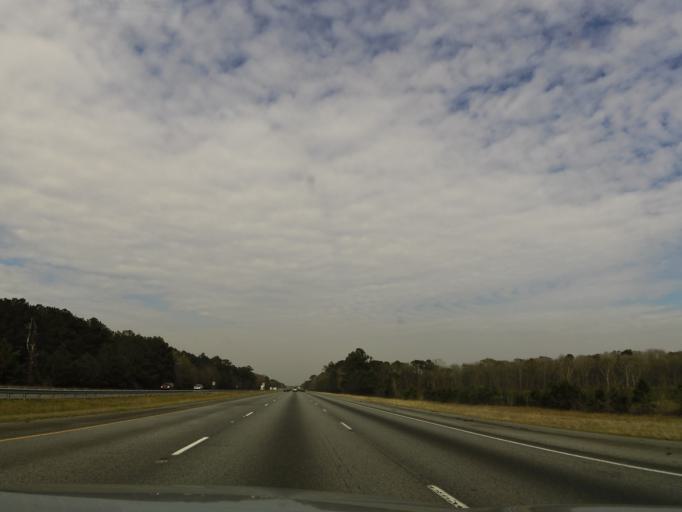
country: US
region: Georgia
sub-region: Liberty County
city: Midway
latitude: 31.6212
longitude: -81.4110
